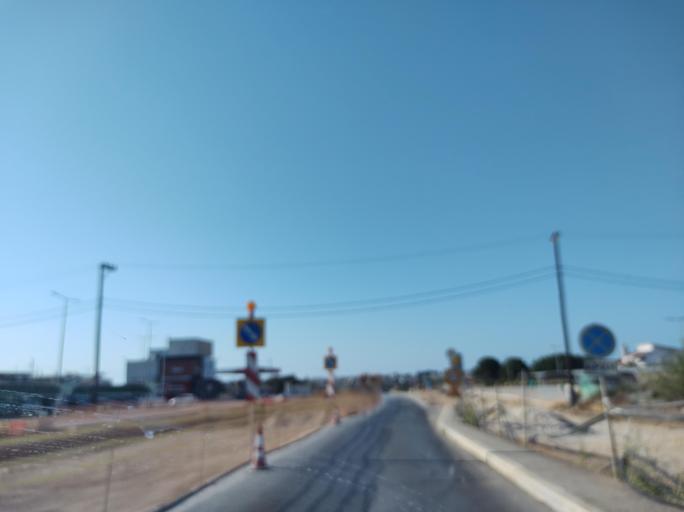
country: GR
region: Crete
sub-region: Nomos Chanias
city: Mournies
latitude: 35.4965
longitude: 24.0183
